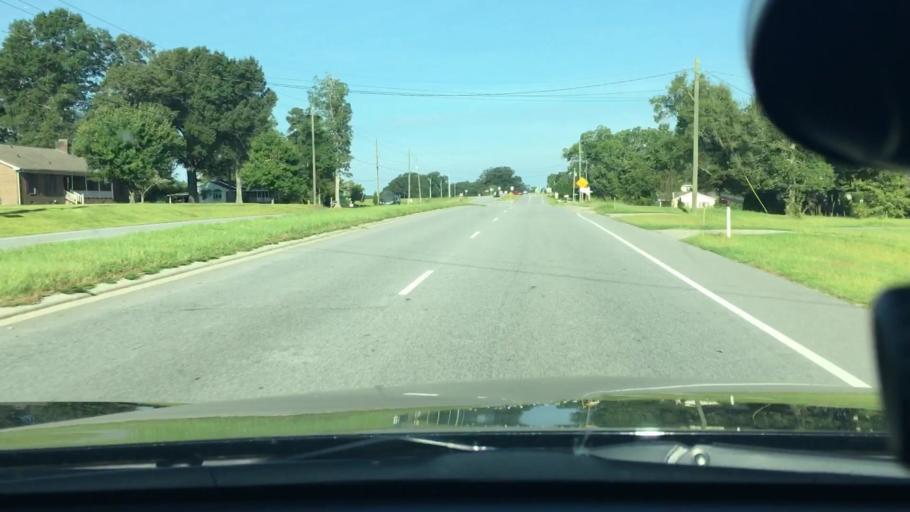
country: US
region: North Carolina
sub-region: Pitt County
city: Greenville
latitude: 35.6280
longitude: -77.4284
